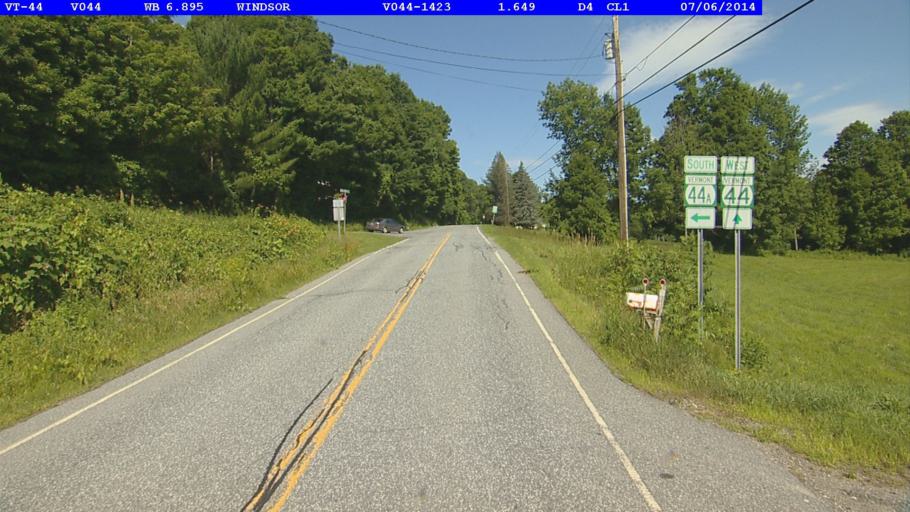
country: US
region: Vermont
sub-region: Windsor County
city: Windsor
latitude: 43.4590
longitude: -72.4236
